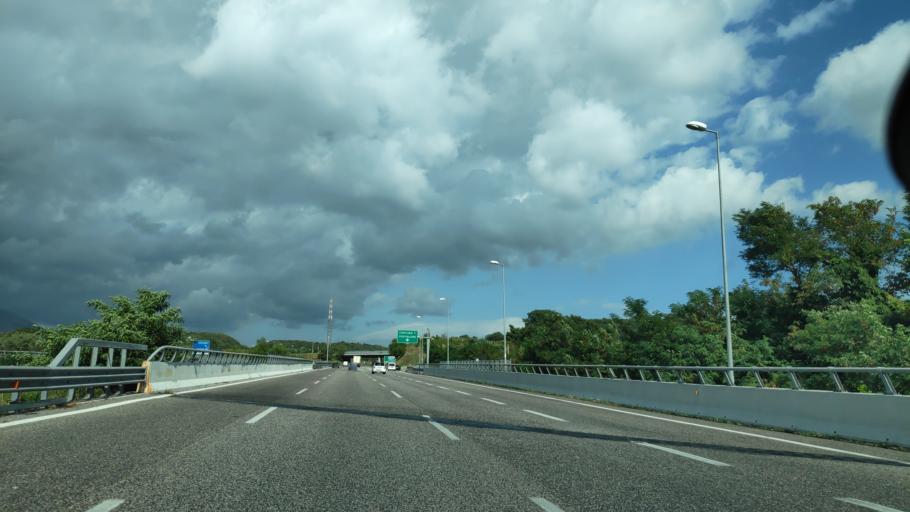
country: IT
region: Campania
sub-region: Provincia di Salerno
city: Contursi Terme
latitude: 40.6285
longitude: 15.2266
